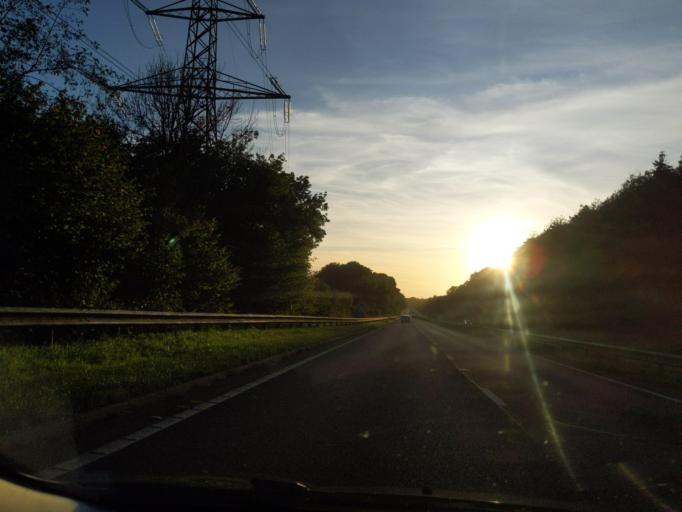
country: GB
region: England
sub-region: Devon
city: Ivybridge
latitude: 50.3943
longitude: -3.8739
